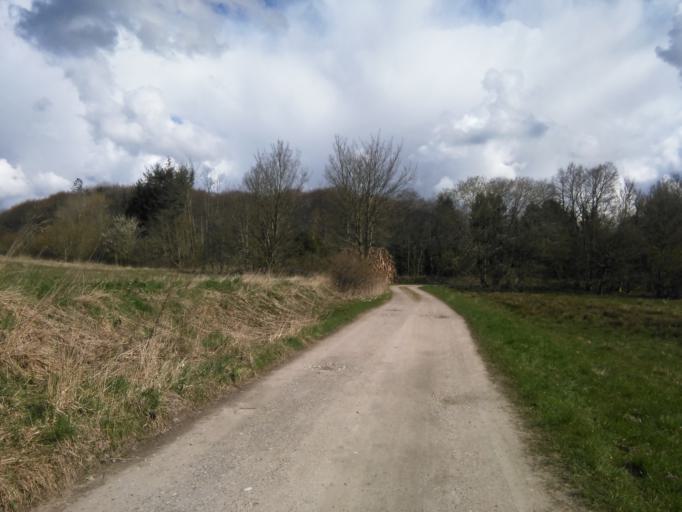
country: DK
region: Central Jutland
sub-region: Arhus Kommune
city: Trige
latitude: 56.2350
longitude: 10.1674
